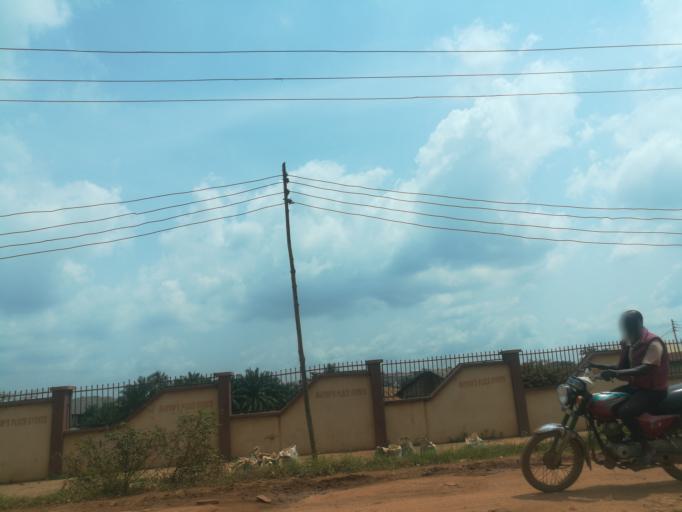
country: NG
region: Oyo
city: Moniya
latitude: 7.4617
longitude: 3.9542
